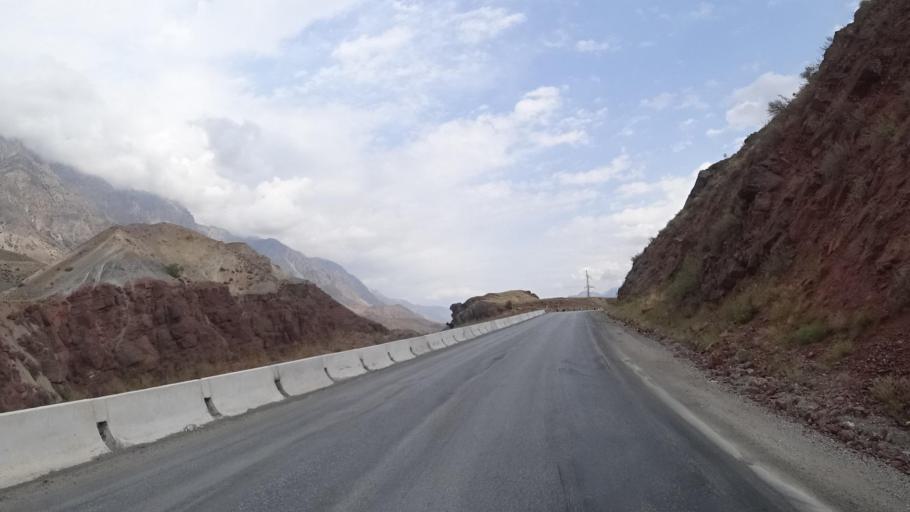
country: KG
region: Jalal-Abad
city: Toktogul
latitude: 41.6277
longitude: 72.6466
